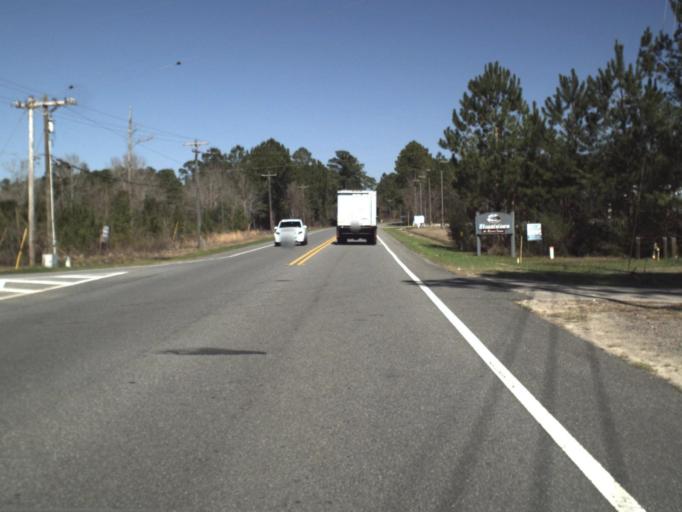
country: US
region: Florida
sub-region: Calhoun County
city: Blountstown
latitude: 30.4311
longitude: -85.0581
